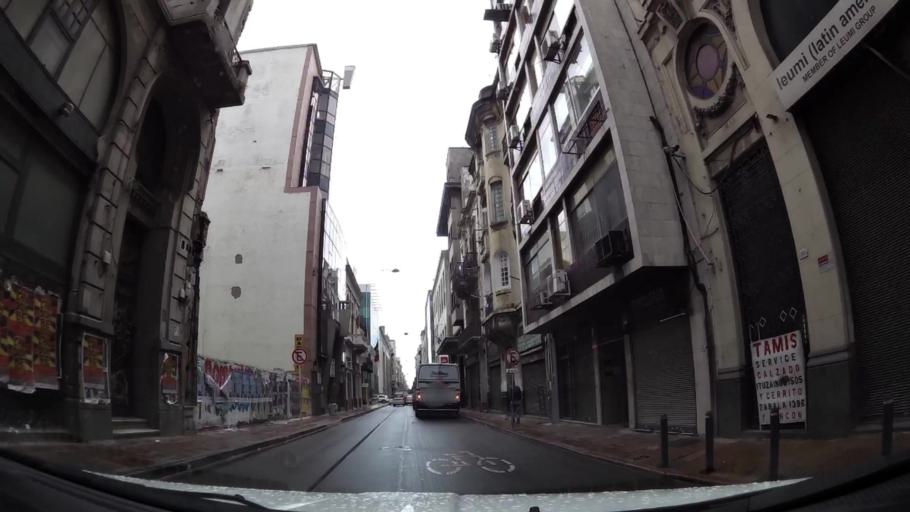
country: UY
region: Montevideo
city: Montevideo
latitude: -34.9056
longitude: -56.2049
